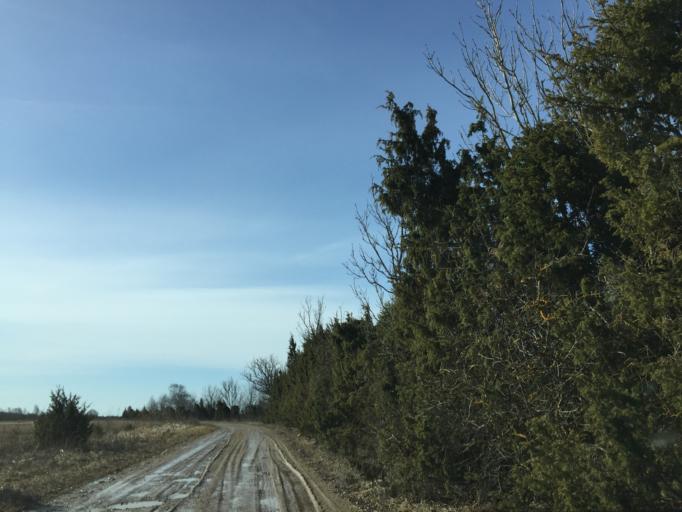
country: EE
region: Laeaene
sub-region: Haapsalu linn
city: Haapsalu
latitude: 58.6535
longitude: 23.5138
